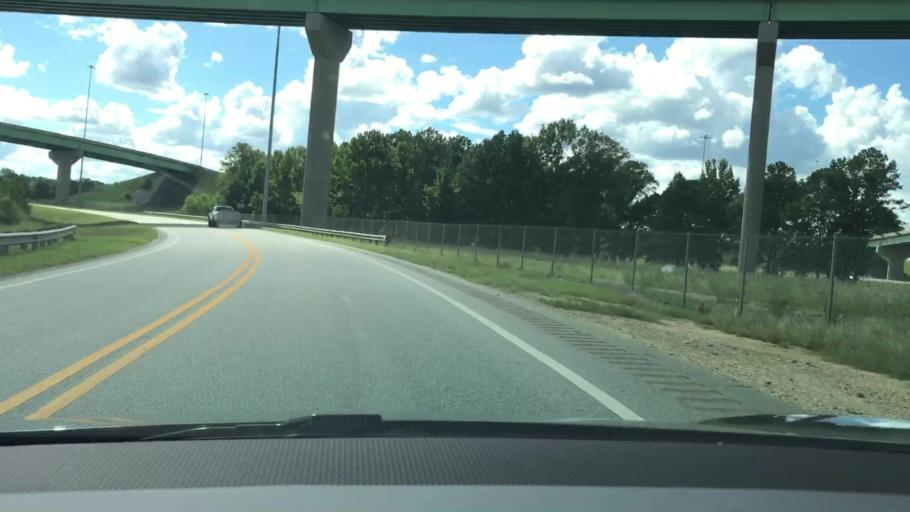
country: US
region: Alabama
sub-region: Montgomery County
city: Pike Road
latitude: 32.3673
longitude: -86.0795
